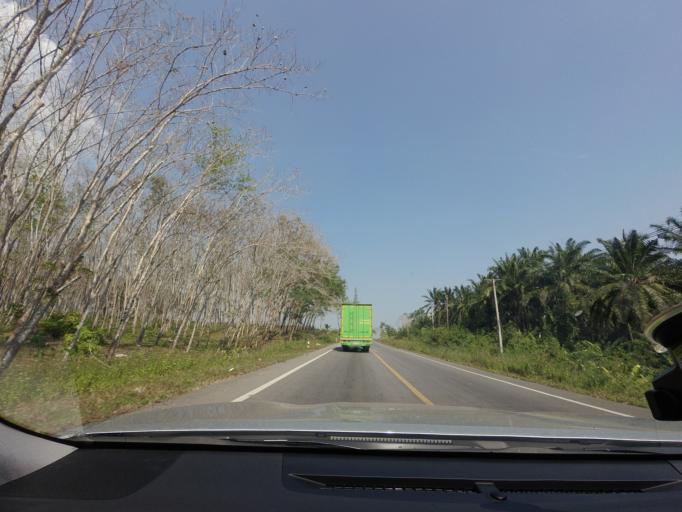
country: TH
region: Krabi
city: Plai Phraya
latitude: 8.5567
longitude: 98.8042
